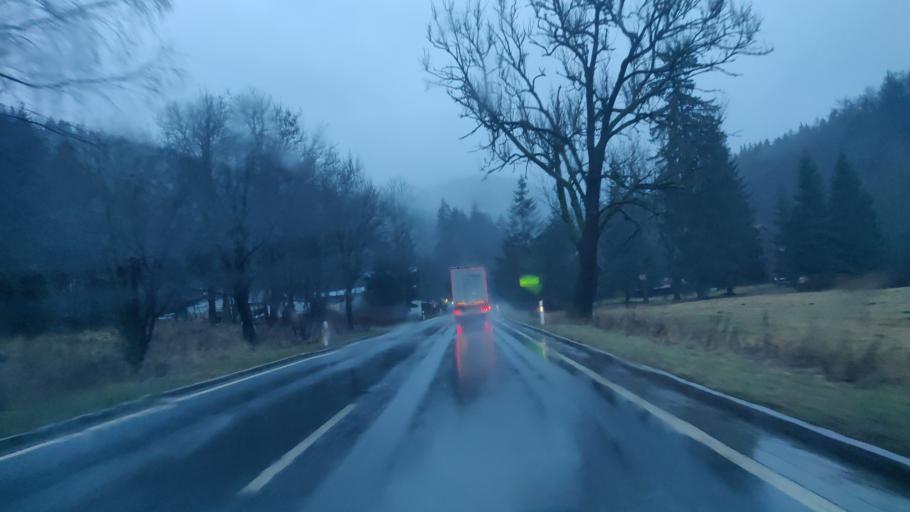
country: DE
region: Lower Saxony
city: Wieda
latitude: 51.6805
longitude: 10.5703
